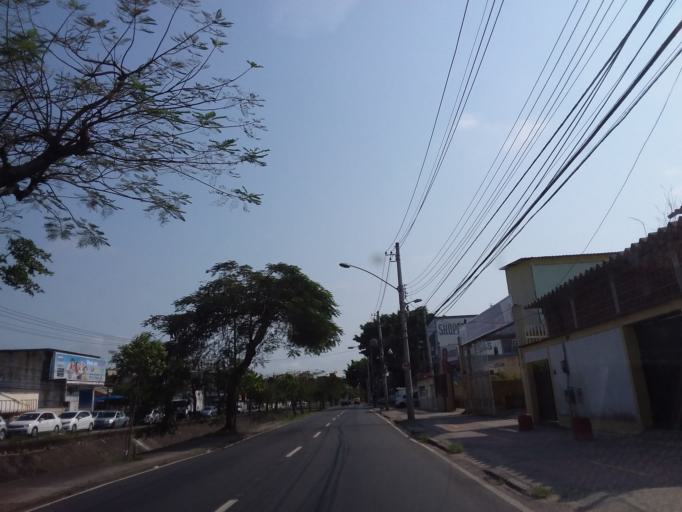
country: BR
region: Rio de Janeiro
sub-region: Nilopolis
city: Nilopolis
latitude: -22.8994
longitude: -43.5422
